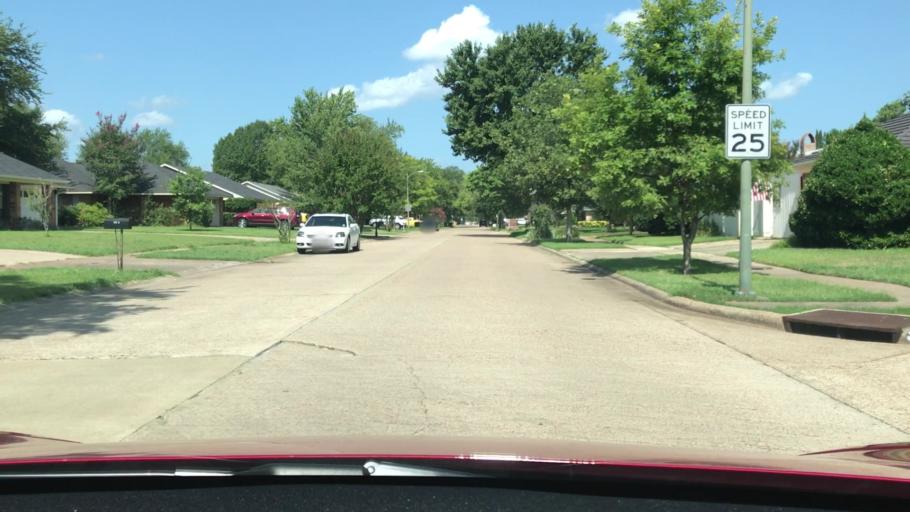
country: US
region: Louisiana
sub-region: Bossier Parish
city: Bossier City
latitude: 32.4197
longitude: -93.7085
